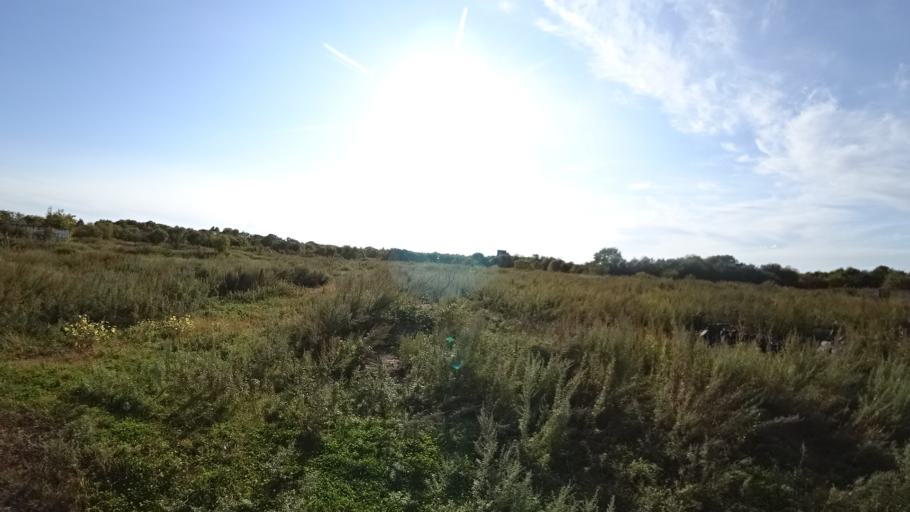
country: RU
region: Amur
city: Arkhara
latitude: 49.3490
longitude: 130.1064
